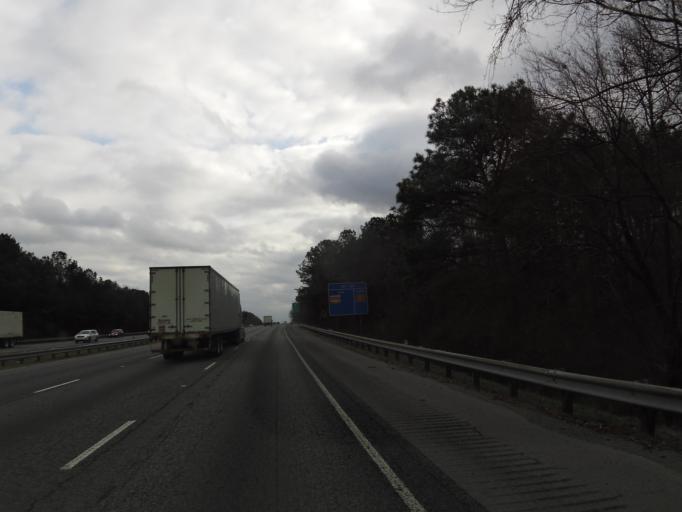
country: US
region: Georgia
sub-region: Gordon County
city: Calhoun
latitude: 34.5981
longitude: -84.9559
